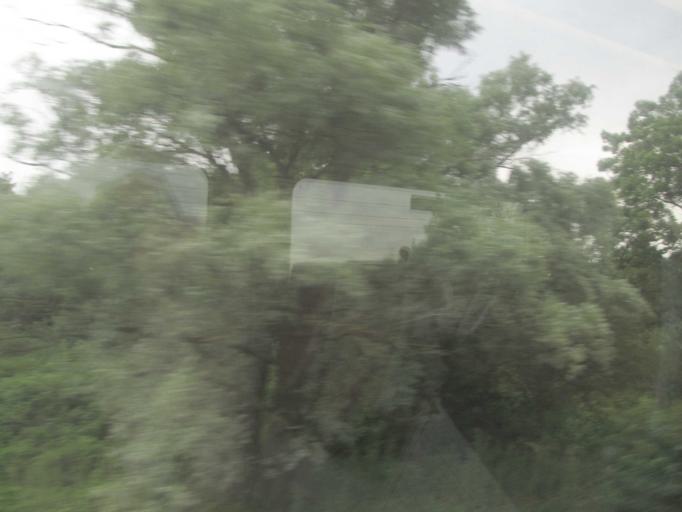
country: GB
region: England
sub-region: Bedford
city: Elstow
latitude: 52.1037
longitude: -0.4803
